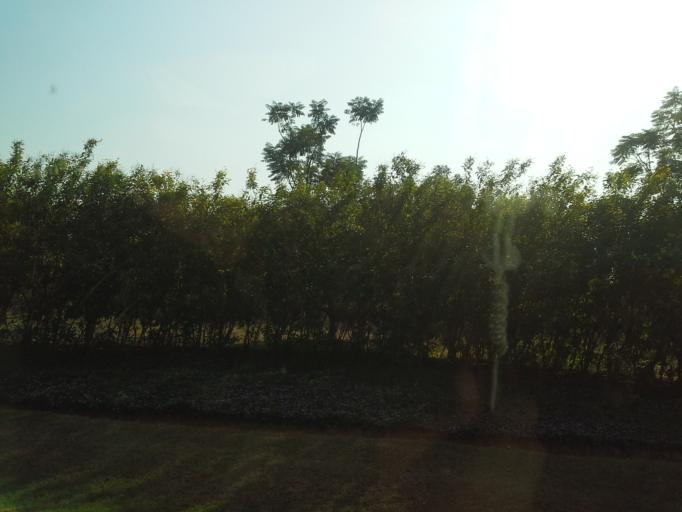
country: IN
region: Telangana
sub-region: Rangareddi
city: Balapur
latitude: 17.2415
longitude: 78.4107
